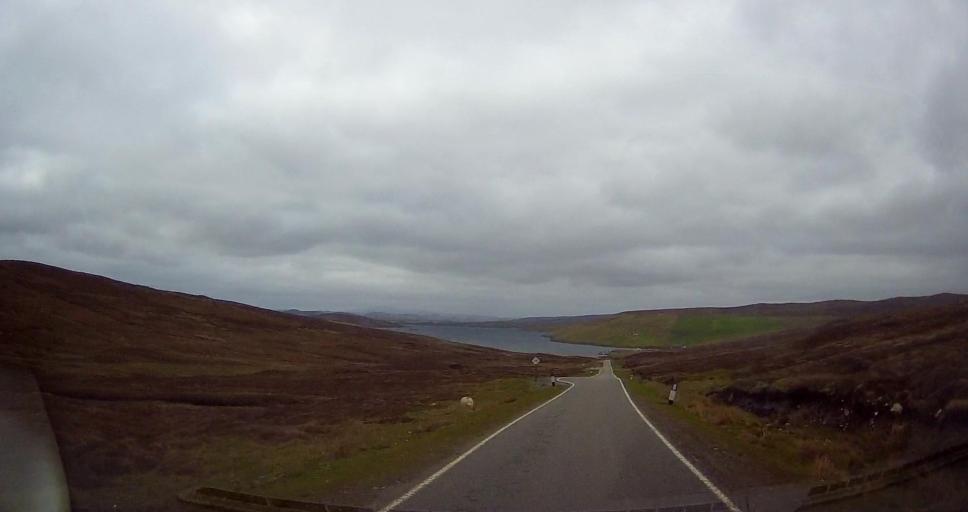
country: GB
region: Scotland
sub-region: Shetland Islands
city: Lerwick
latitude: 60.3245
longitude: -1.3391
